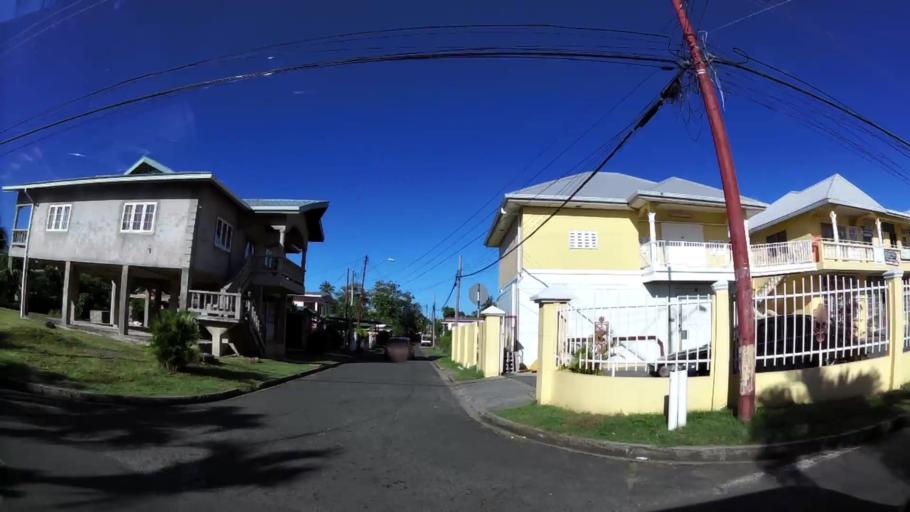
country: TT
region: Tobago
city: Scarborough
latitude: 11.1569
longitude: -60.8205
